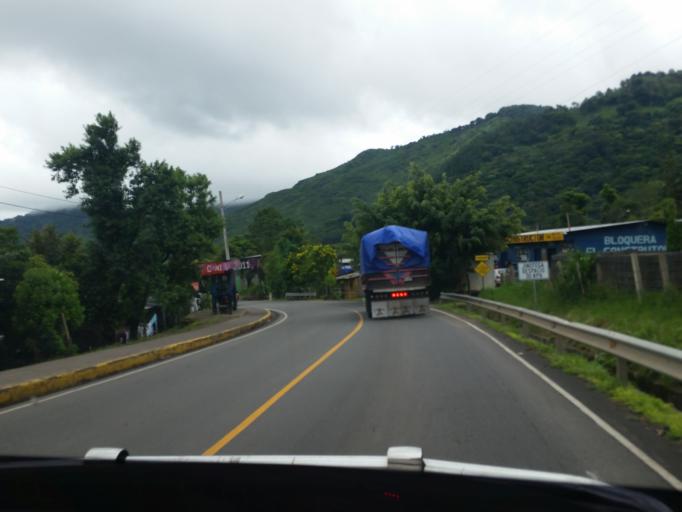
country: NI
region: Jinotega
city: Jinotega
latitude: 13.0819
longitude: -85.9929
